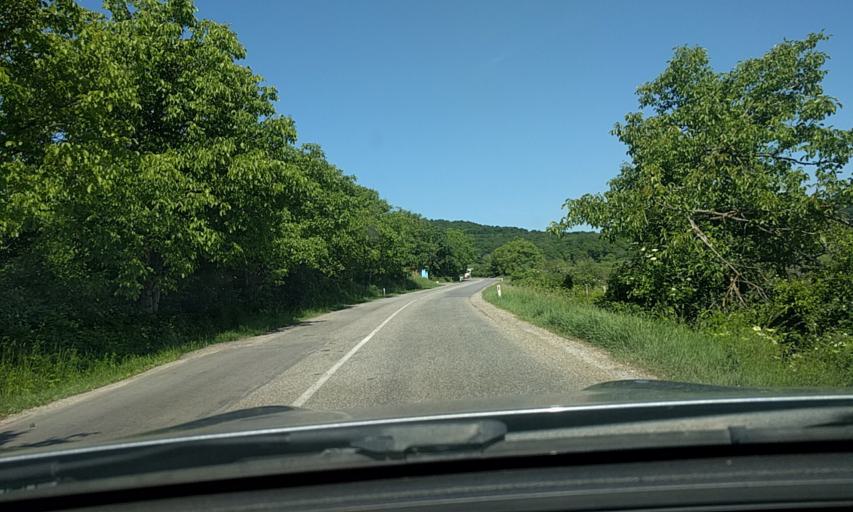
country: RO
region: Bistrita-Nasaud
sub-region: Comuna Dumitra
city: Dumitra
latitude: 47.1805
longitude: 24.4895
